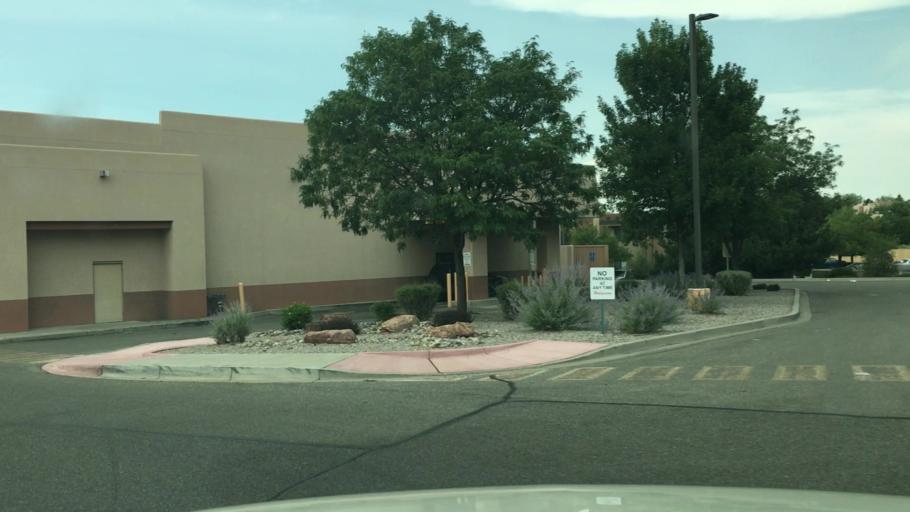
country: US
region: New Mexico
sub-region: Santa Fe County
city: Santa Fe
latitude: 35.6472
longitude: -105.9547
